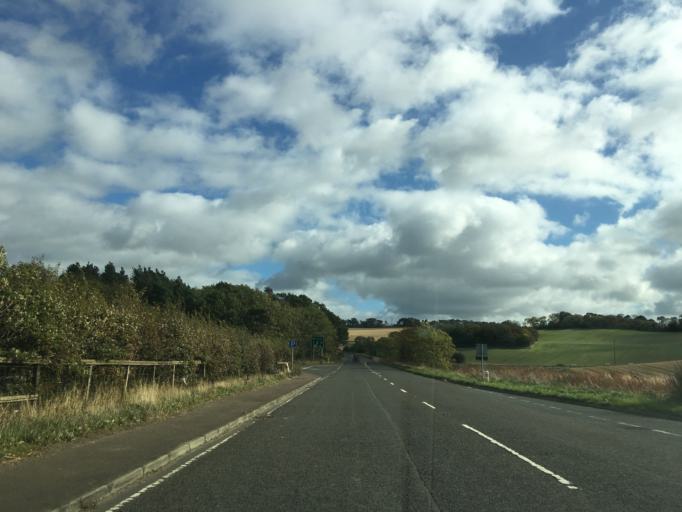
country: GB
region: Scotland
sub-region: Midlothian
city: Dalkeith
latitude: 55.8905
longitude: -3.0293
